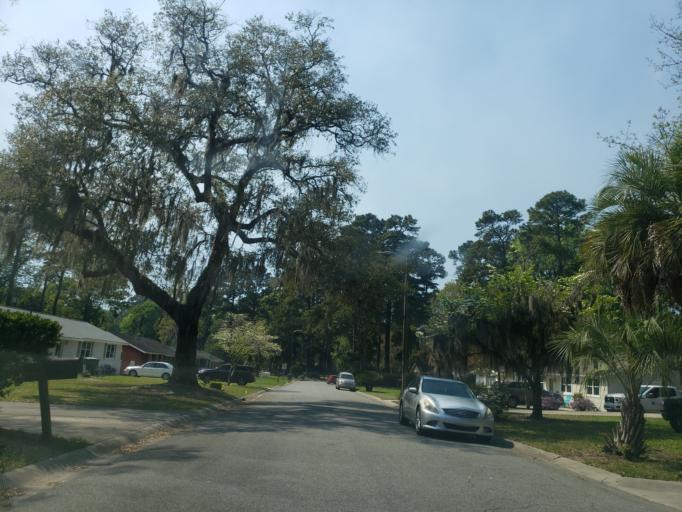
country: US
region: Georgia
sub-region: Chatham County
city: Thunderbolt
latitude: 32.0113
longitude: -81.0708
